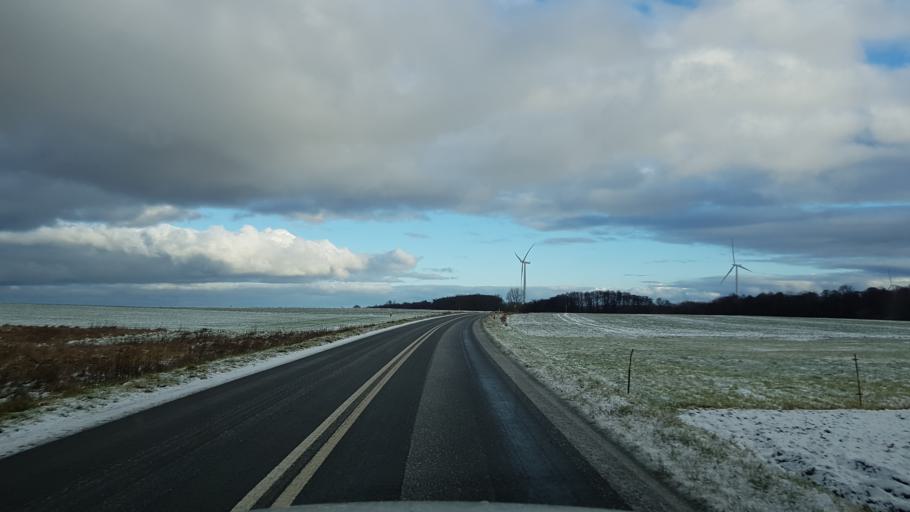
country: PL
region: West Pomeranian Voivodeship
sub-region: Powiat gryficki
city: Karnice
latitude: 54.0356
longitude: 15.0560
